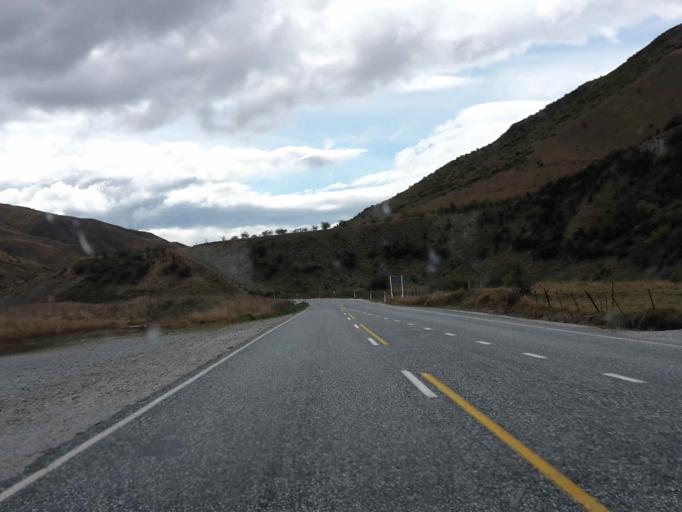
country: NZ
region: Otago
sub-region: Queenstown-Lakes District
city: Arrowtown
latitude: -44.9191
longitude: 168.9727
